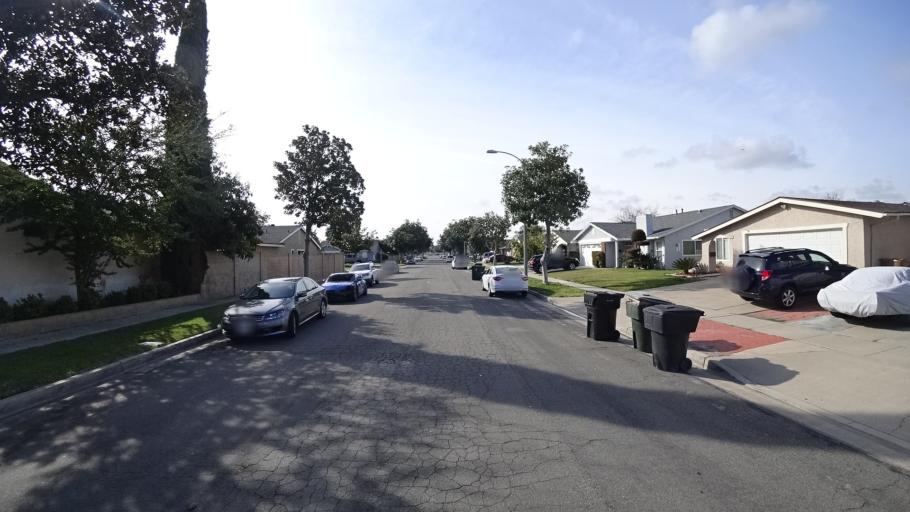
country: US
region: California
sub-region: Orange County
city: Stanton
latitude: 33.8310
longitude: -117.9726
